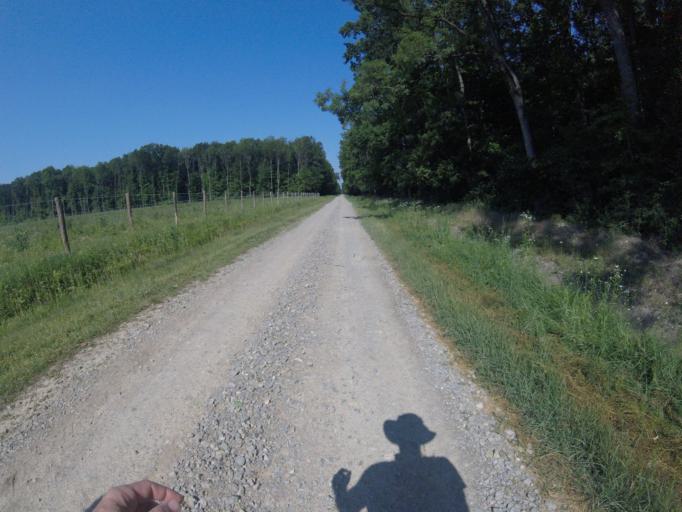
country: HU
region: Baranya
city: Szigetvar
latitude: 45.9831
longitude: 17.8166
